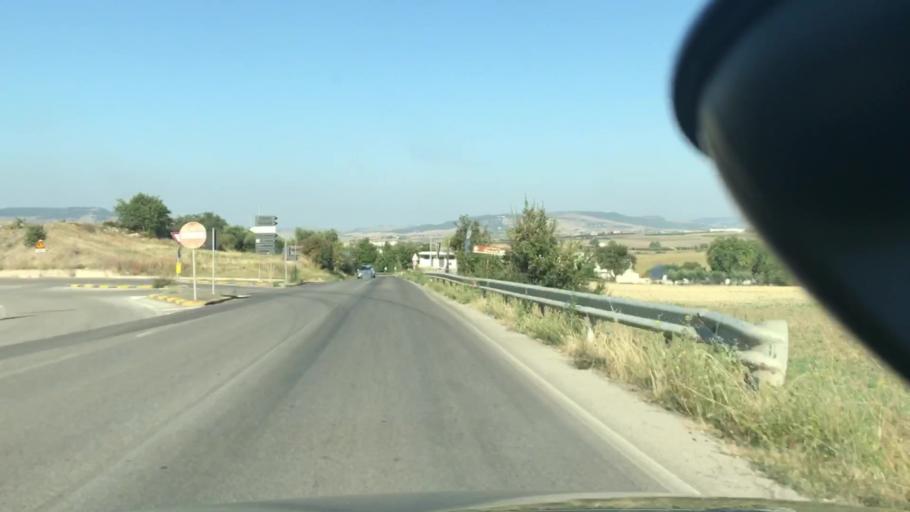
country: IT
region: Basilicate
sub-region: Provincia di Matera
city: La Martella
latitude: 40.6602
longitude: 16.5656
